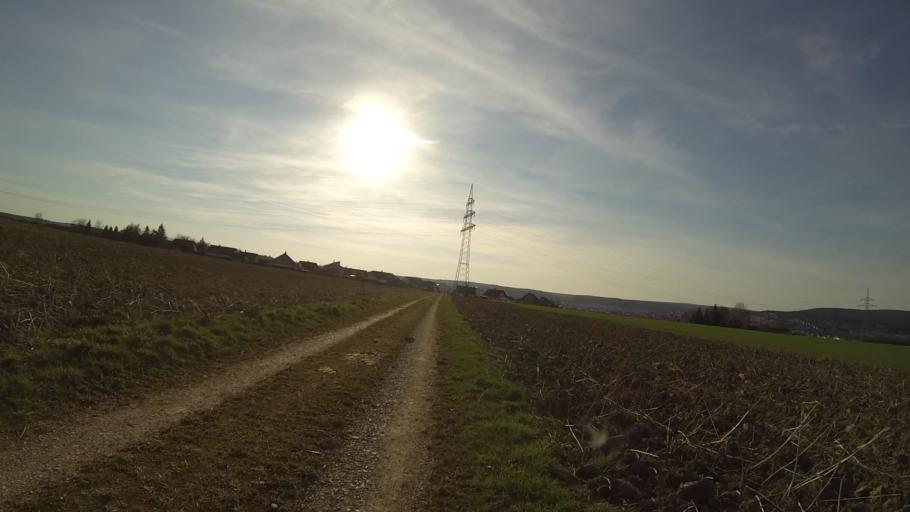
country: DE
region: Baden-Wuerttemberg
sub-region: Regierungsbezirk Stuttgart
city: Herbrechtingen
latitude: 48.6192
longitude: 10.1944
